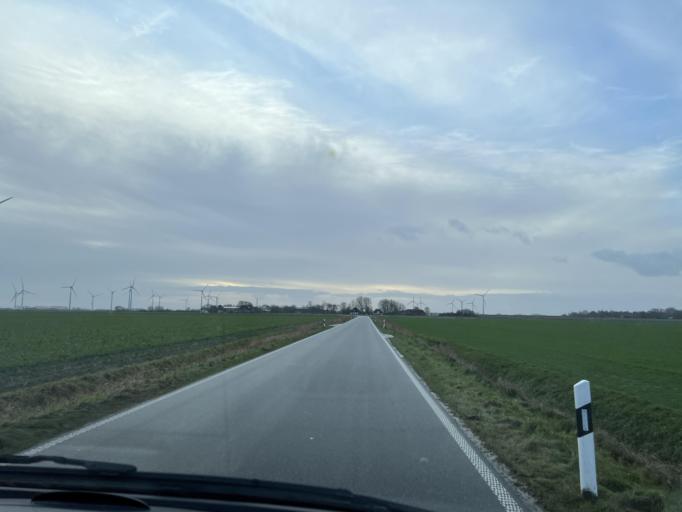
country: DE
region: Schleswig-Holstein
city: Norddeich
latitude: 54.1940
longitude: 8.8925
